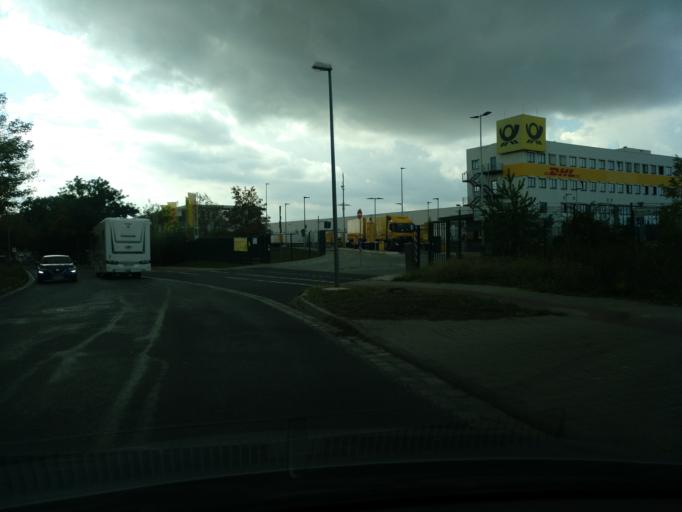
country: DE
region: Brandenburg
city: Petershagen
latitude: 52.4860
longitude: 13.7808
